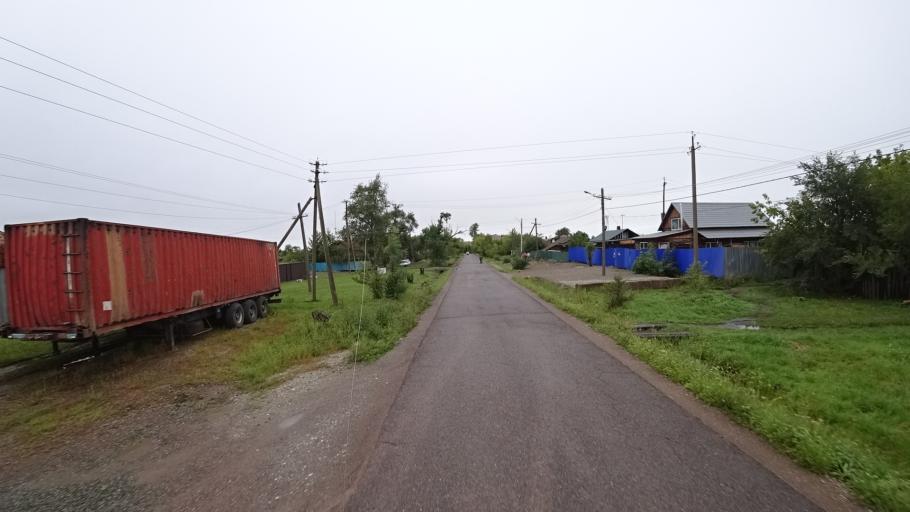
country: RU
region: Primorskiy
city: Monastyrishche
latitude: 44.2018
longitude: 132.4617
